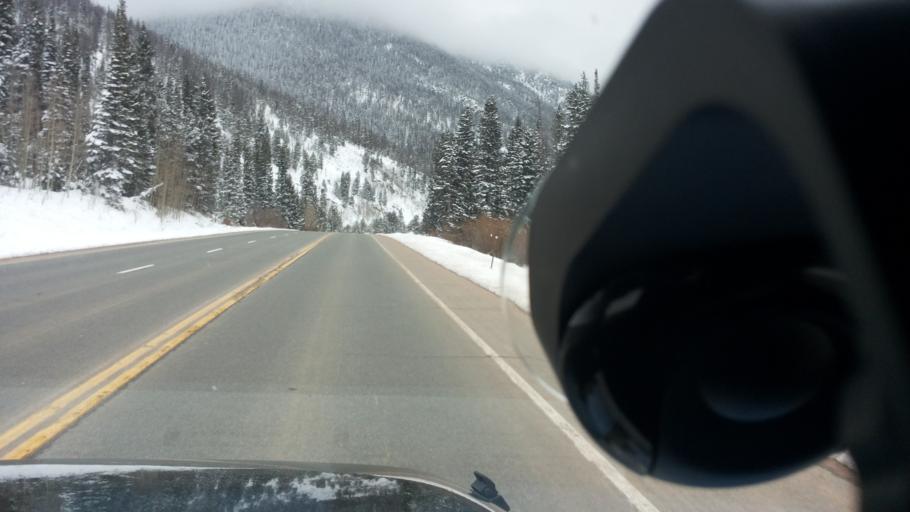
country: US
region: Colorado
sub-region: Clear Creek County
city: Georgetown
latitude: 39.7751
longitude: -105.7960
